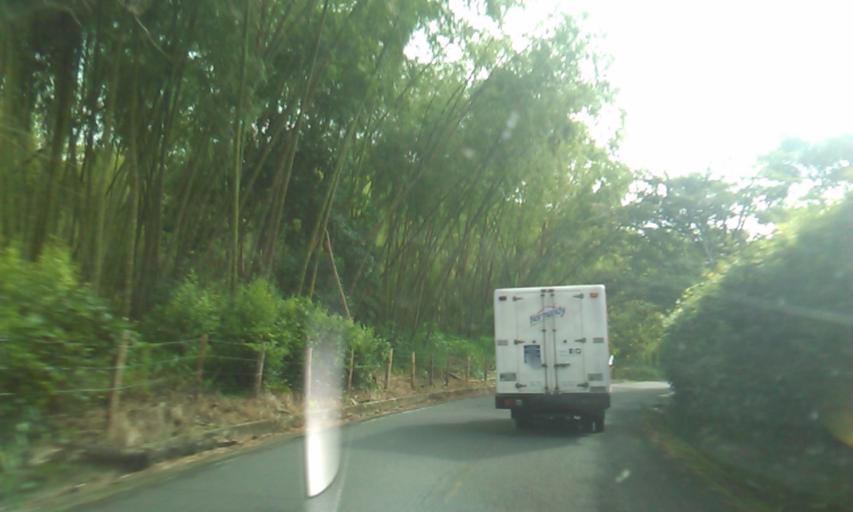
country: CO
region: Quindio
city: Cordoba
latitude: 4.4126
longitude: -75.6991
